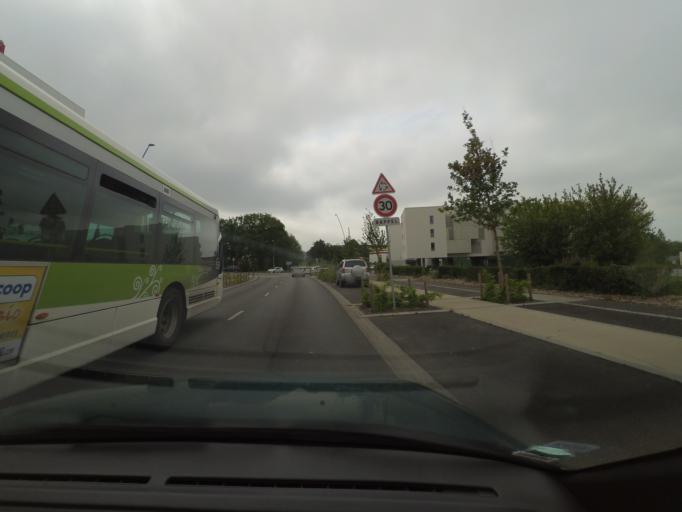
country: FR
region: Pays de la Loire
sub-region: Departement de la Vendee
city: La Roche-sur-Yon
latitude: 46.6789
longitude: -1.4404
